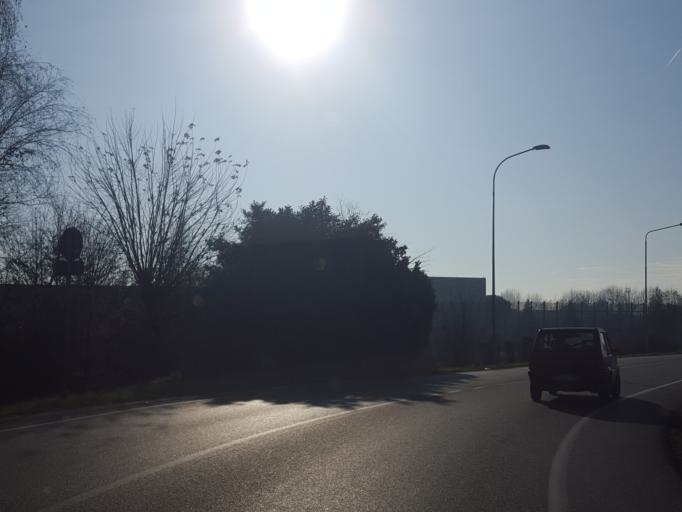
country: IT
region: Veneto
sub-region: Provincia di Vicenza
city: Vicenza
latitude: 45.5542
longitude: 11.5782
